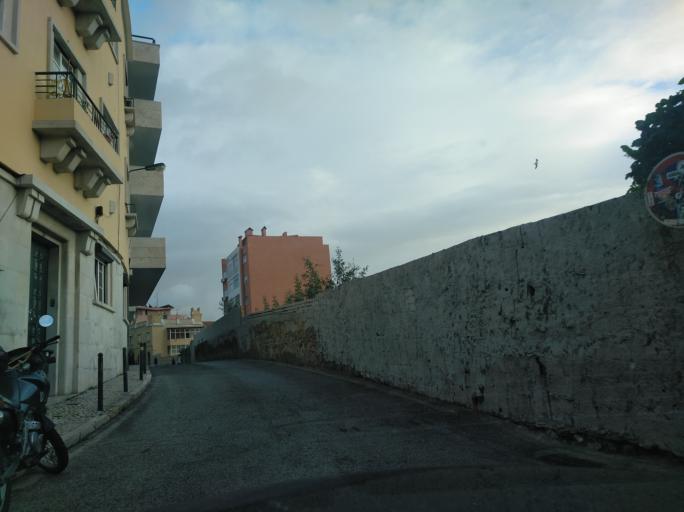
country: PT
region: Lisbon
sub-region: Lisbon
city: Lisbon
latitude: 38.7190
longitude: -9.1334
